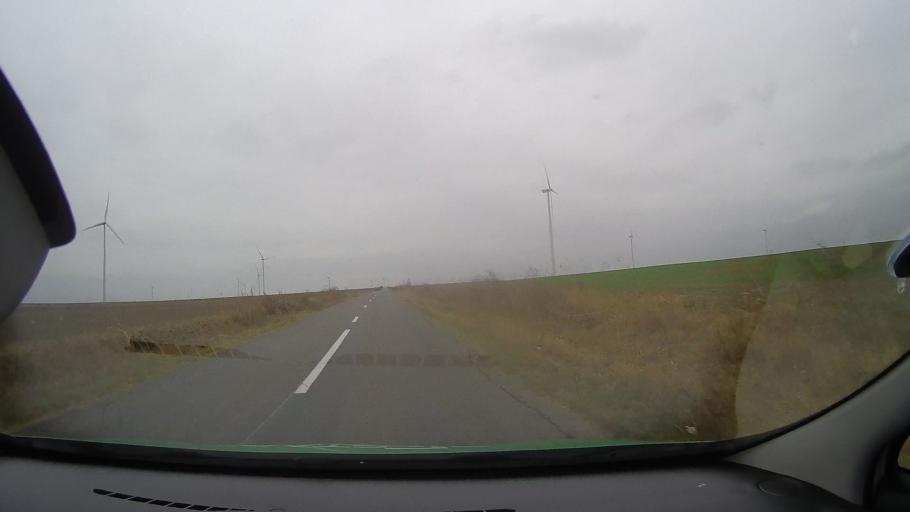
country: RO
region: Constanta
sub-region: Comuna Pantelimon
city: Pantelimon
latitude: 44.5040
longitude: 28.3490
